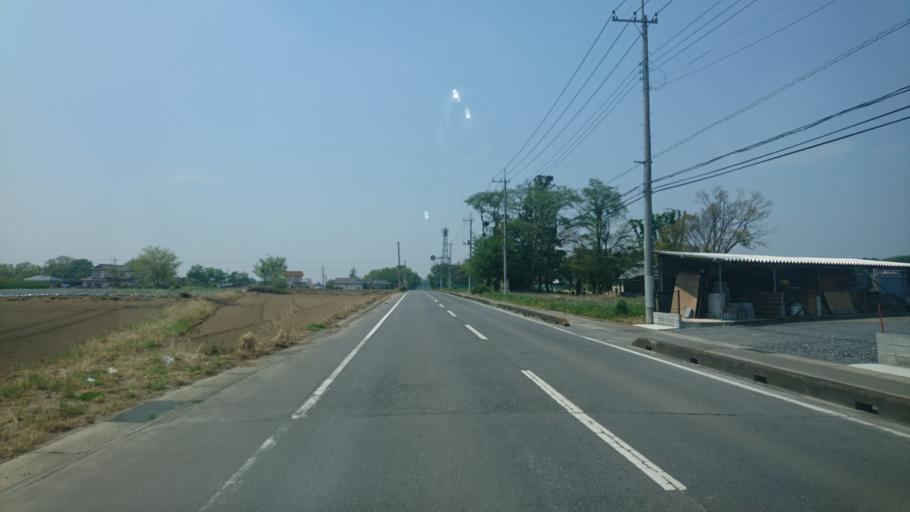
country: JP
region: Ibaraki
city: Shimodate
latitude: 36.2552
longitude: 139.9714
